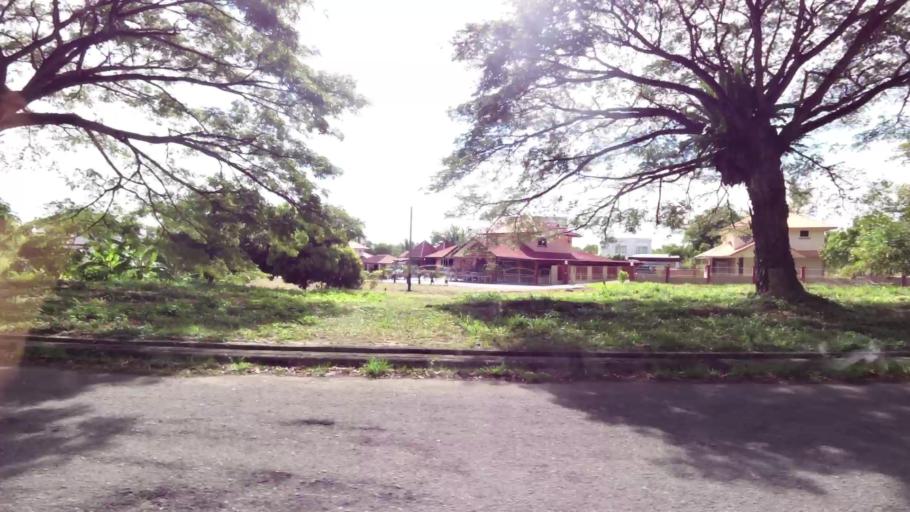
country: BN
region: Brunei and Muara
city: Bandar Seri Begawan
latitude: 4.9310
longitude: 114.9072
